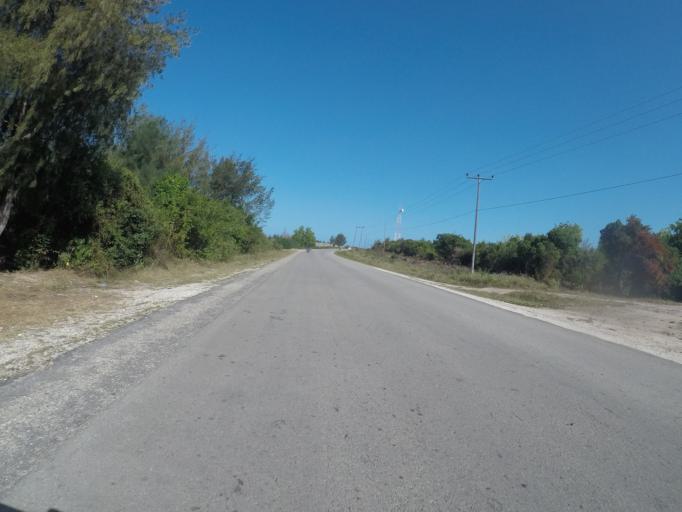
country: TZ
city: Kiwengwa
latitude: -6.1639
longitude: 39.5226
